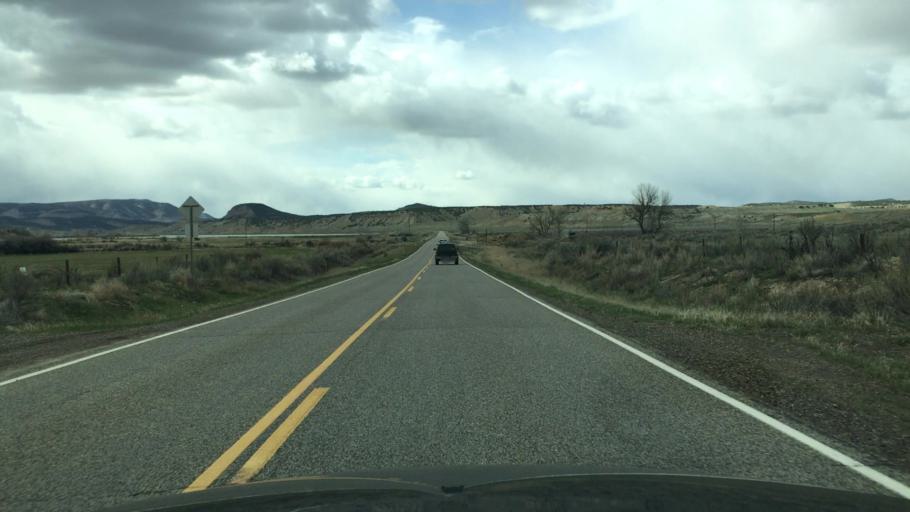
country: US
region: Colorado
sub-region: Rio Blanco County
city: Meeker
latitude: 40.0814
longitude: -108.1915
